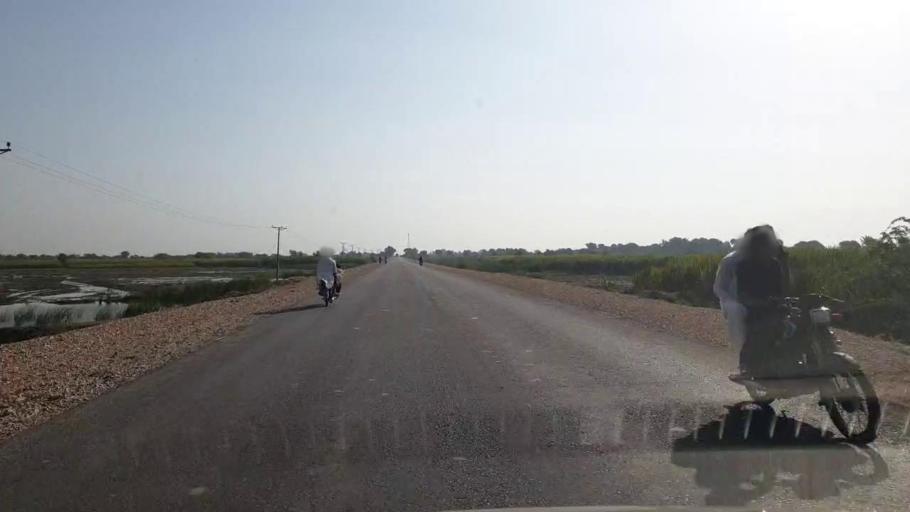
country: PK
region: Sindh
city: Badin
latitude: 24.6588
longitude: 68.9366
